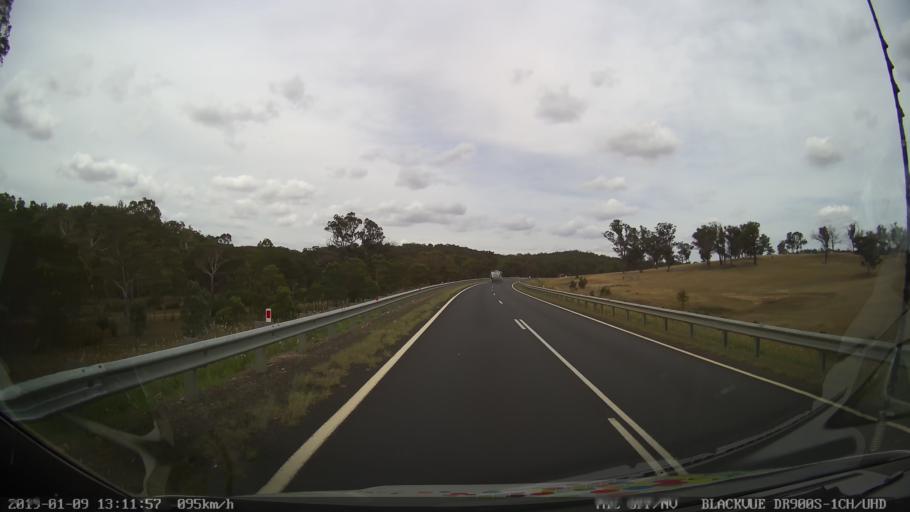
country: AU
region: New South Wales
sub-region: Armidale Dumaresq
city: Armidale
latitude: -30.5406
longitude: 151.7336
